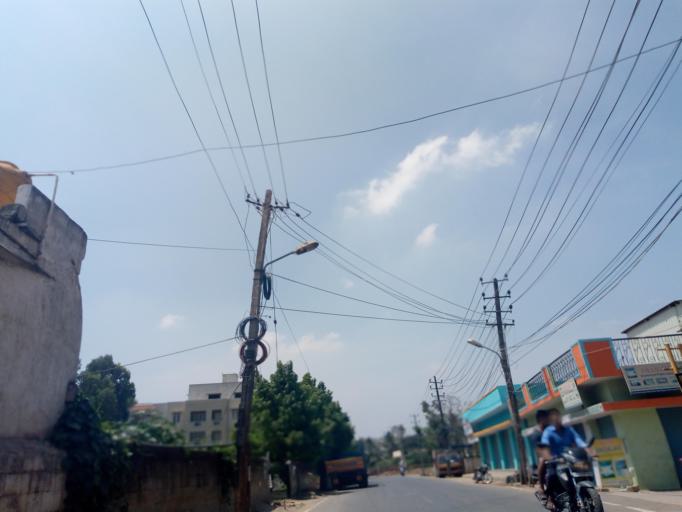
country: IN
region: Karnataka
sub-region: Bangalore Urban
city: Bangalore
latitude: 12.8952
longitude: 77.6509
